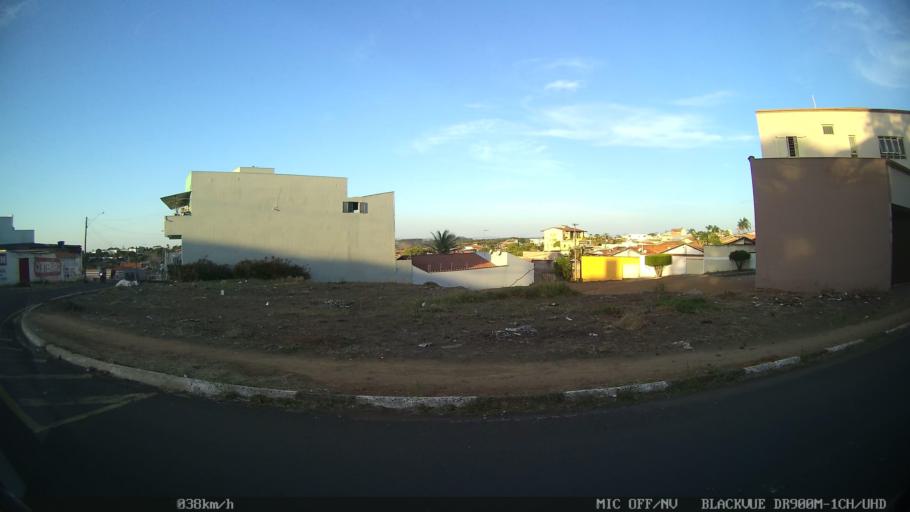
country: BR
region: Sao Paulo
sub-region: Franca
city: Franca
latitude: -20.5038
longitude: -47.3977
